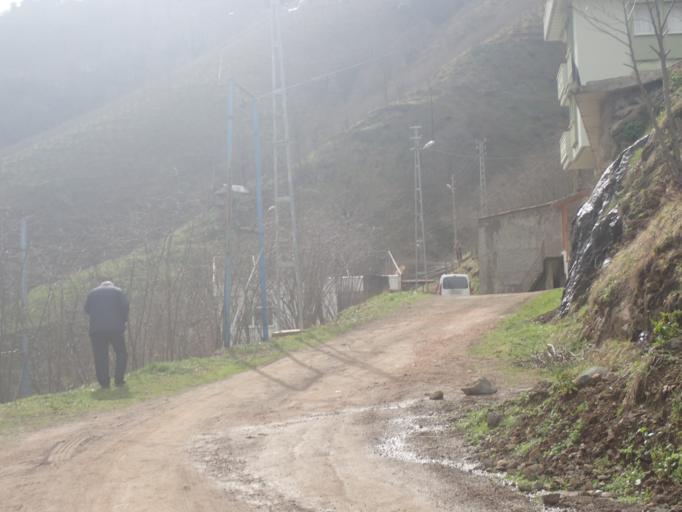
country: TR
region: Ordu
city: Camas
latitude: 40.9019
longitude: 37.5762
